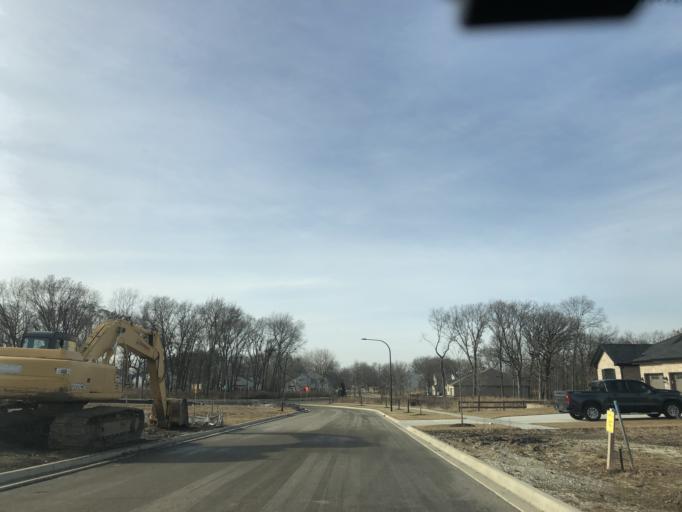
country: US
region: Illinois
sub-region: DuPage County
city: Woodridge
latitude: 41.7206
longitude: -88.0115
